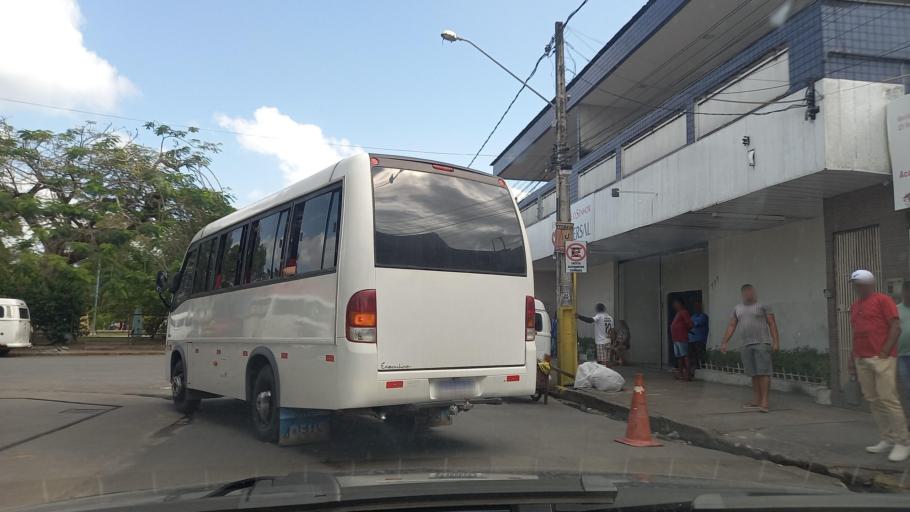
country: BR
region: Pernambuco
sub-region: Goiana
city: Goiana
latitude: -7.5614
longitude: -34.9994
